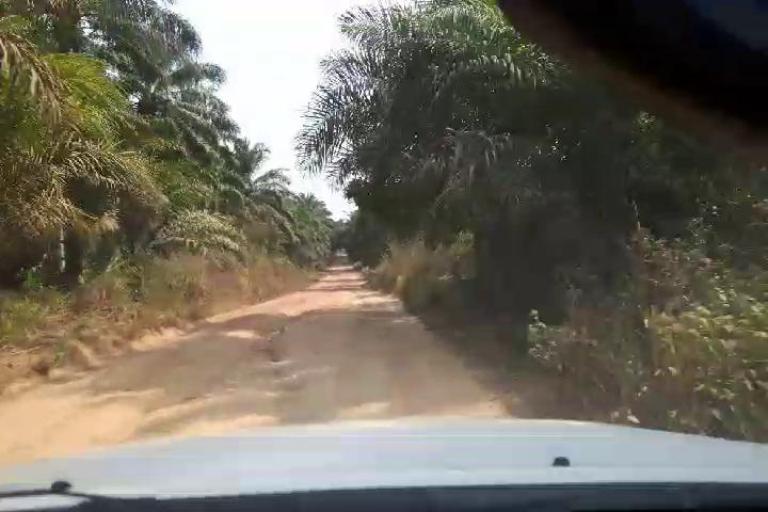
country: SL
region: Northern Province
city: Masingbi
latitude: 8.7890
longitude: -11.8705
